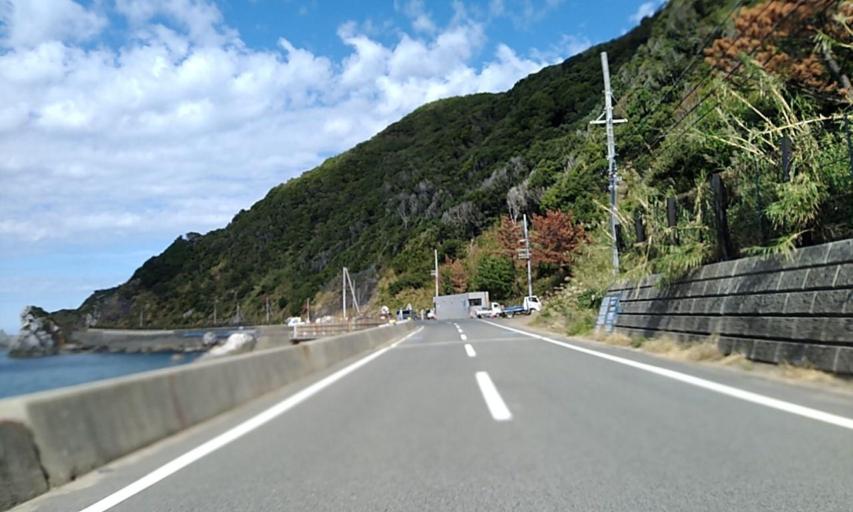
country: JP
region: Wakayama
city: Gobo
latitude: 33.9711
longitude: 135.0795
